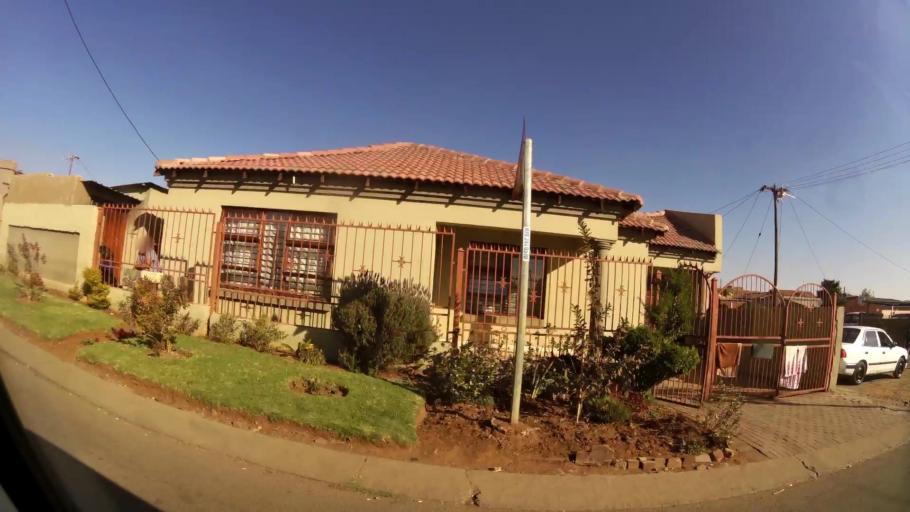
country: ZA
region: Gauteng
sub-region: City of Tshwane Metropolitan Municipality
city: Cullinan
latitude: -25.7237
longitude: 28.3833
